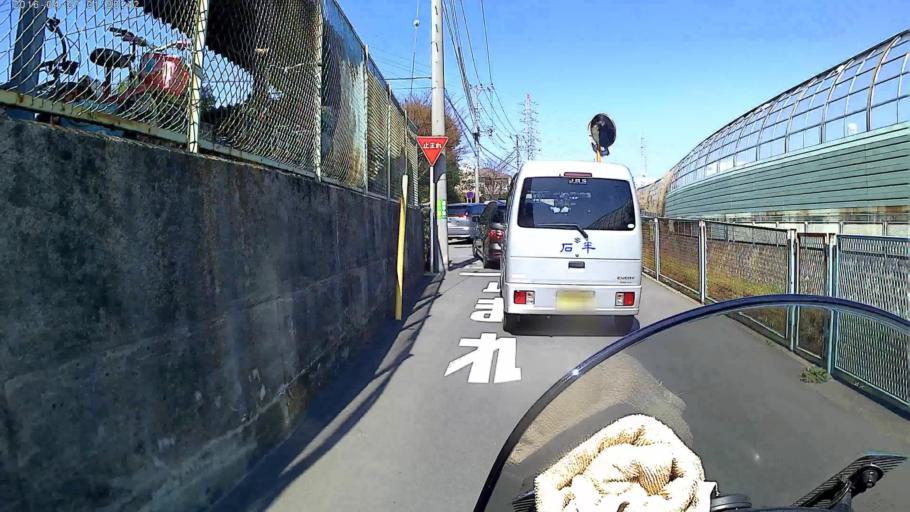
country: JP
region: Kanagawa
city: Yokohama
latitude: 35.4231
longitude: 139.5391
